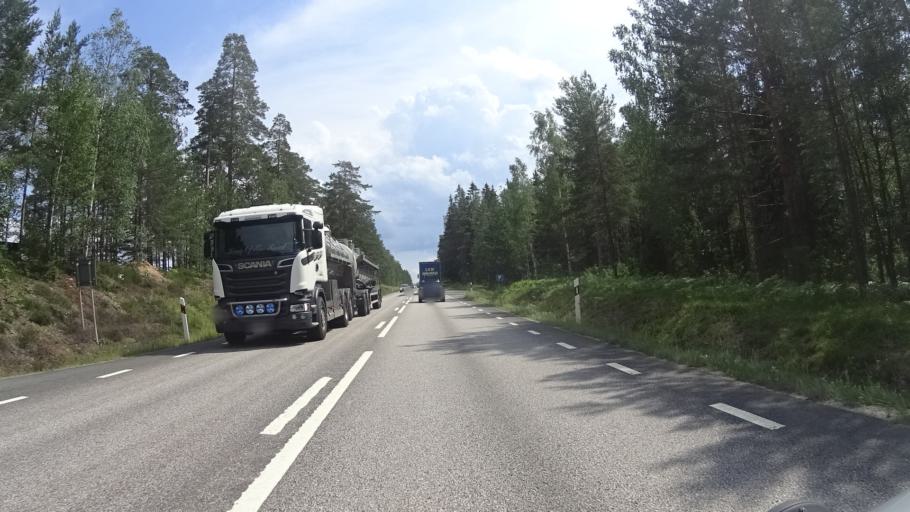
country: SE
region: Kalmar
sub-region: Hultsfreds Kommun
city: Hultsfred
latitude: 57.4819
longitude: 15.8325
